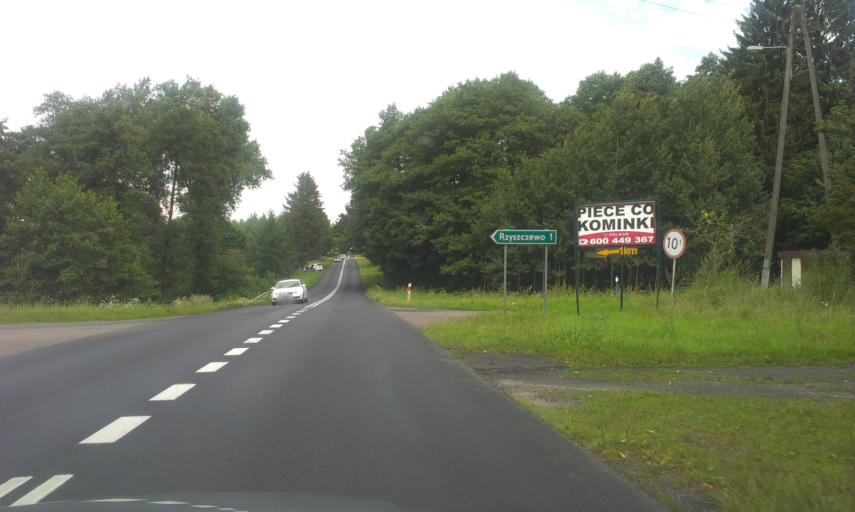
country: PL
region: West Pomeranian Voivodeship
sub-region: Powiat bialogardzki
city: Bialogard
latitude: 53.9250
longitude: 16.0641
